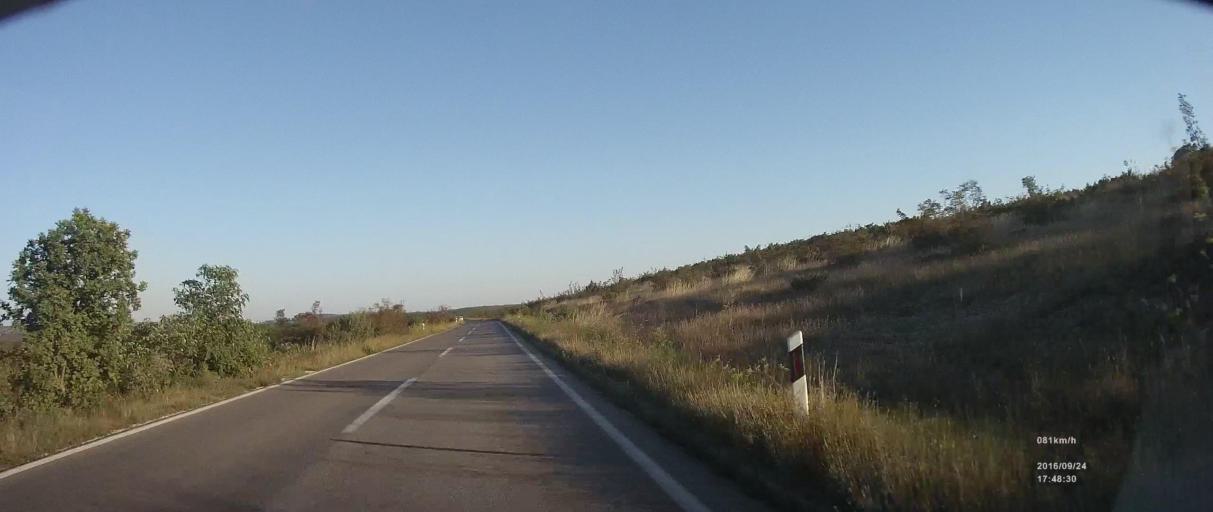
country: HR
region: Zadarska
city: Polaca
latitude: 44.0641
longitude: 15.5373
